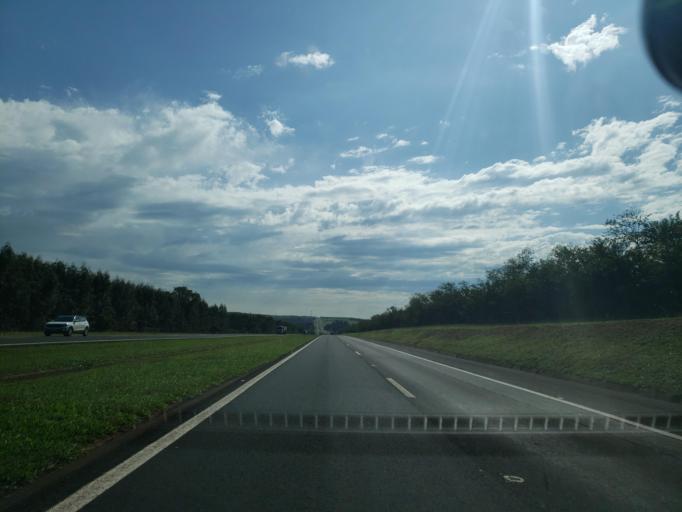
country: BR
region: Sao Paulo
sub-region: Pirajui
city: Pirajui
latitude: -21.9045
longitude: -49.5250
